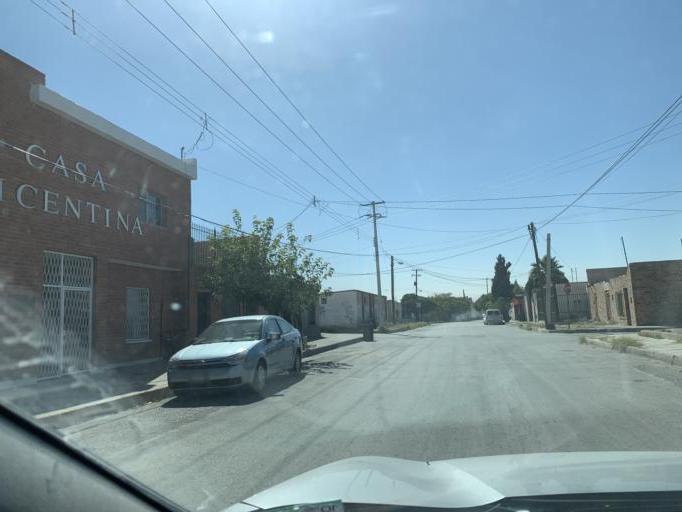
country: MX
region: Chihuahua
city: Ciudad Juarez
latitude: 31.7223
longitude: -106.4639
